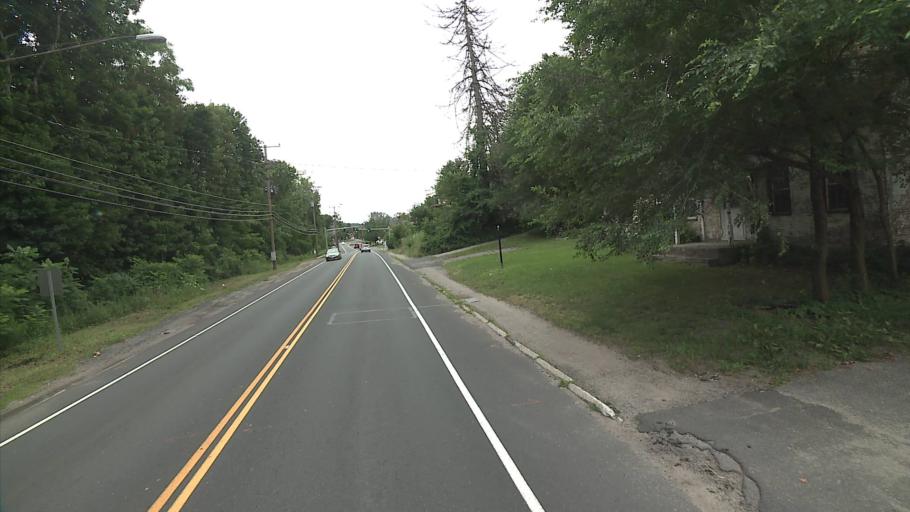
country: US
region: Connecticut
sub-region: Litchfield County
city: Winsted
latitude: 41.9262
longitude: -73.0597
